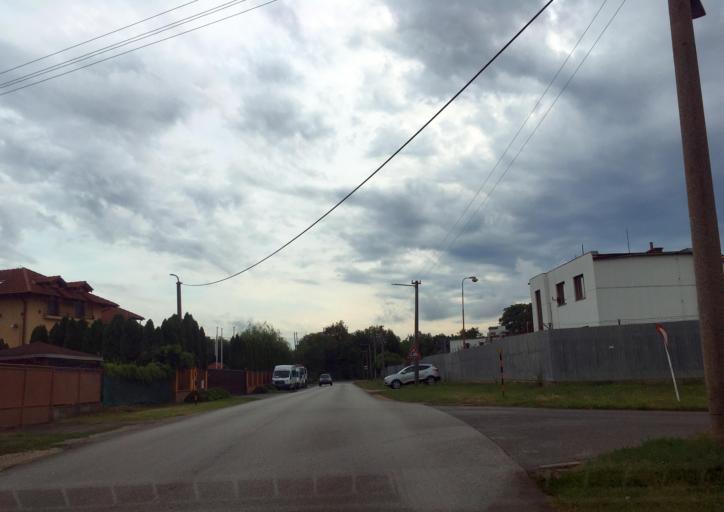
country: SK
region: Nitriansky
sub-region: Okres Nove Zamky
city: Sturovo
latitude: 47.8095
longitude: 18.7003
